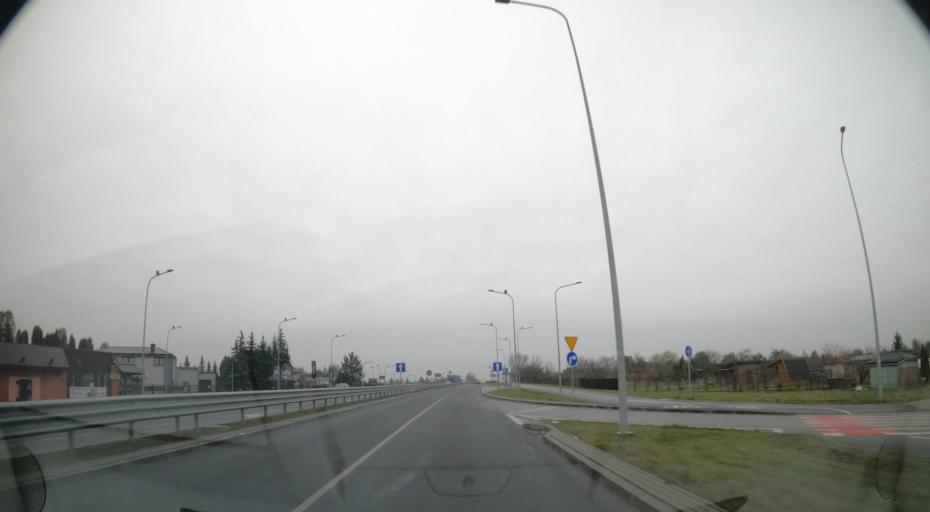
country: PL
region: Masovian Voivodeship
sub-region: Radom
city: Radom
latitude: 51.3881
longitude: 21.1917
